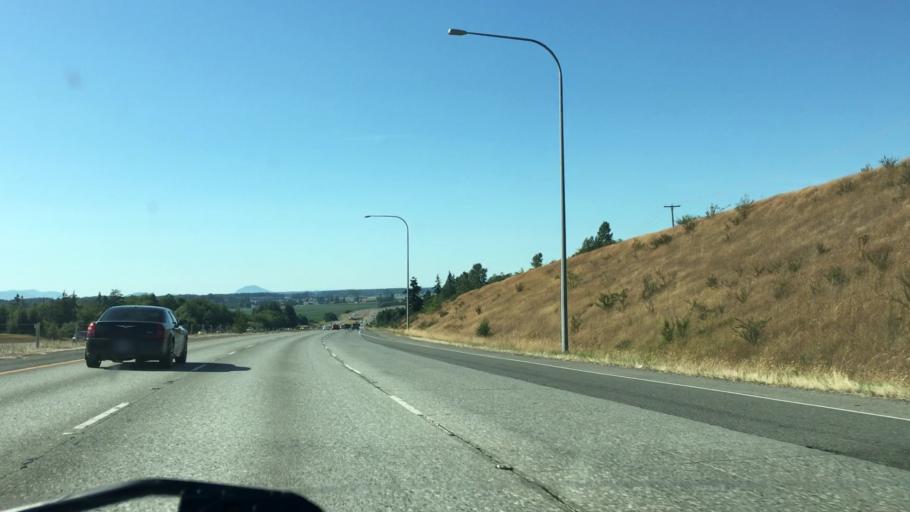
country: US
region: Washington
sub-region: Snohomish County
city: Stanwood
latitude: 48.3121
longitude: -122.3211
